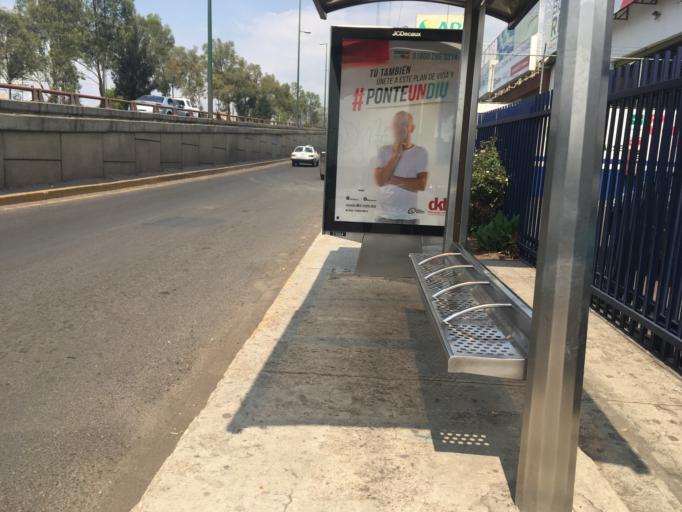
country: MX
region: Michoacan
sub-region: Tarimbaro
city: Real Hacienda (Metropolis)
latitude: 19.7263
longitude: -101.2080
